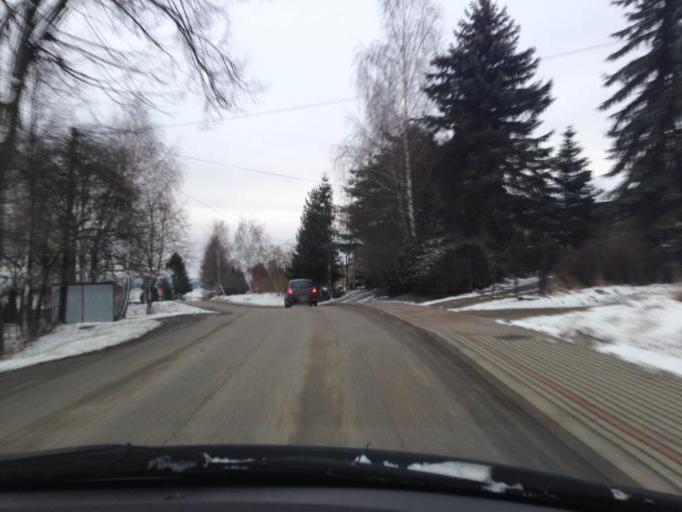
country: PL
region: Lesser Poland Voivodeship
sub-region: Powiat gorlicki
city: Moszczenica
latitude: 49.7210
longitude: 21.1090
